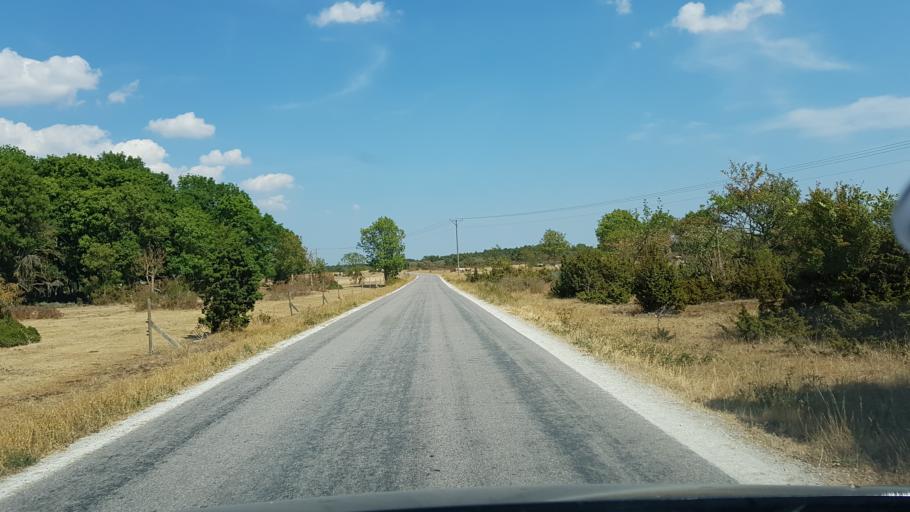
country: SE
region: Gotland
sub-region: Gotland
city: Visby
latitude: 57.6574
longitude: 18.3650
